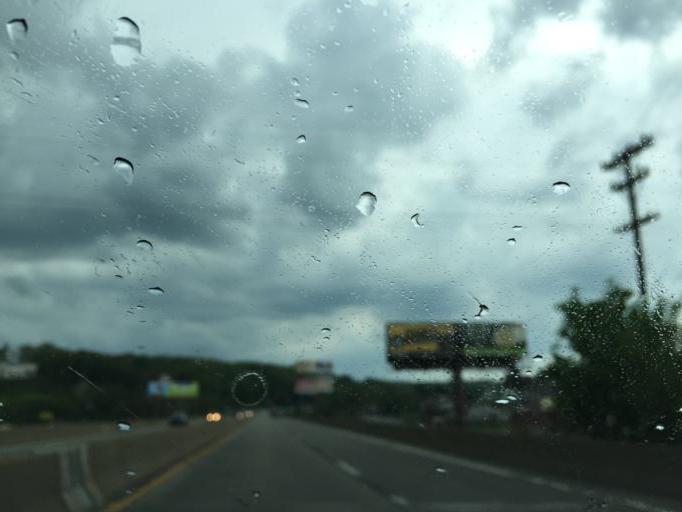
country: US
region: Pennsylvania
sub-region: Westmoreland County
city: Southwest Greensburg
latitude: 40.2851
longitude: -79.5447
